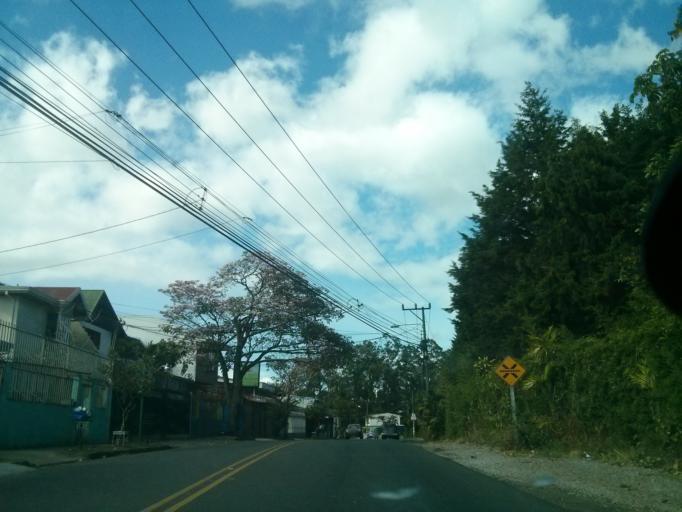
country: CR
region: San Jose
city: Curridabat
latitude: 9.9196
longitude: -84.0328
